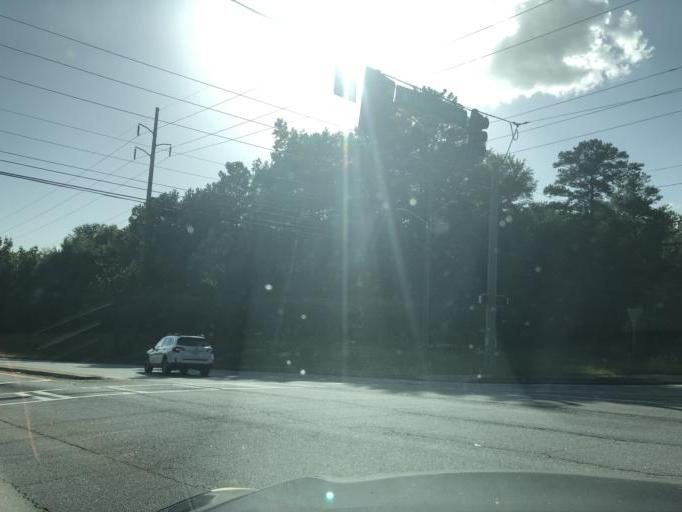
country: US
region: Georgia
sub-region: Muscogee County
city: Columbus
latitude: 32.5099
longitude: -84.8922
